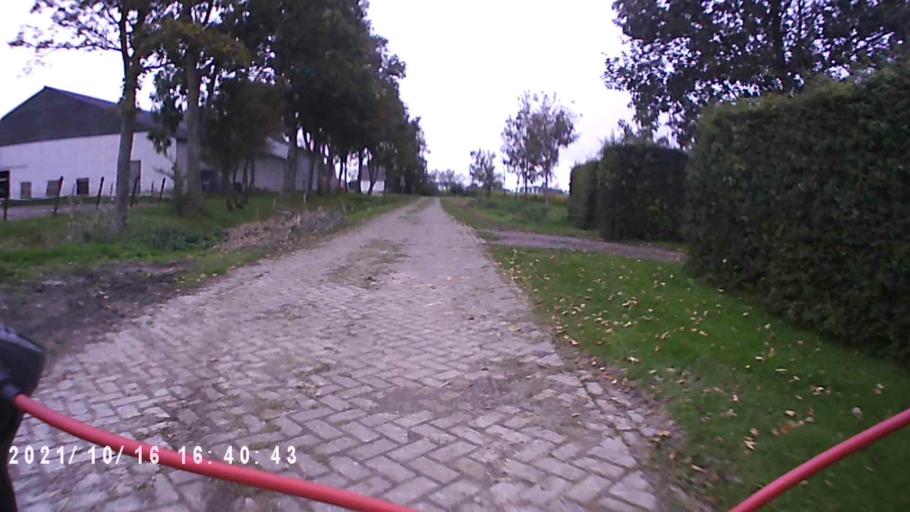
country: NL
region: Friesland
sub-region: Gemeente Dongeradeel
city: Anjum
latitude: 53.3779
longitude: 6.1455
